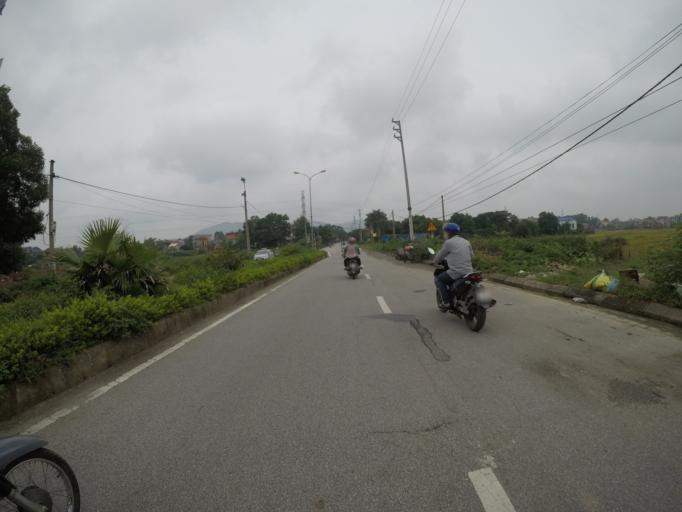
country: VN
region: Ha Noi
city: Soc Son
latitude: 21.2757
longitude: 105.8490
